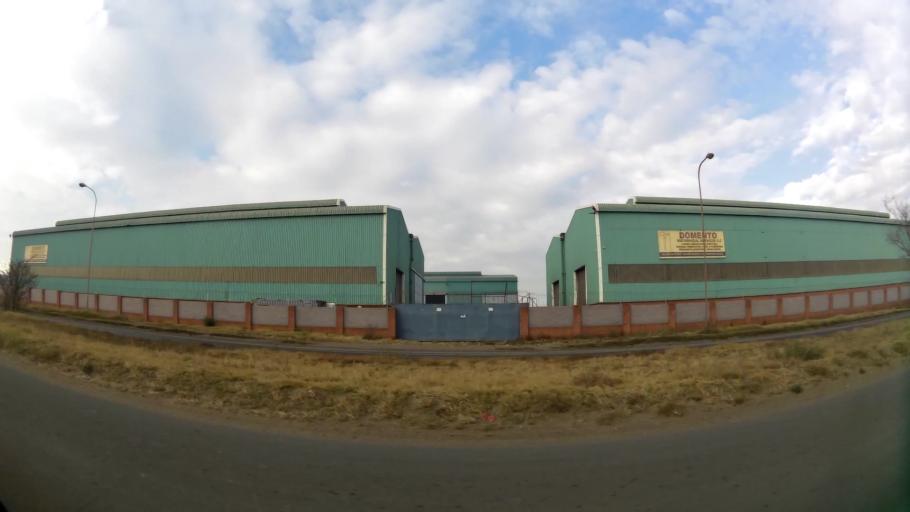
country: ZA
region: Gauteng
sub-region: Sedibeng District Municipality
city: Vanderbijlpark
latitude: -26.6740
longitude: 27.8019
